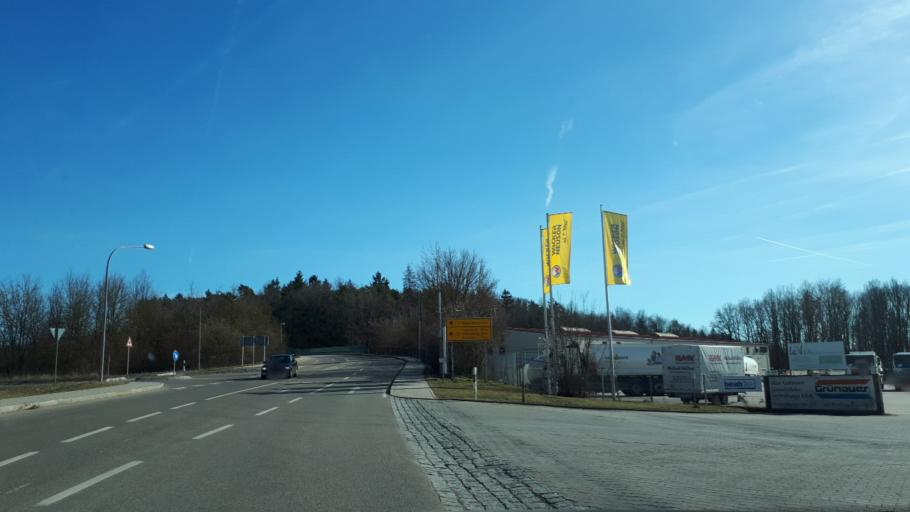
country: DE
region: Bavaria
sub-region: Upper Palatinate
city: Pentling
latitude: 48.9733
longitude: 12.0621
